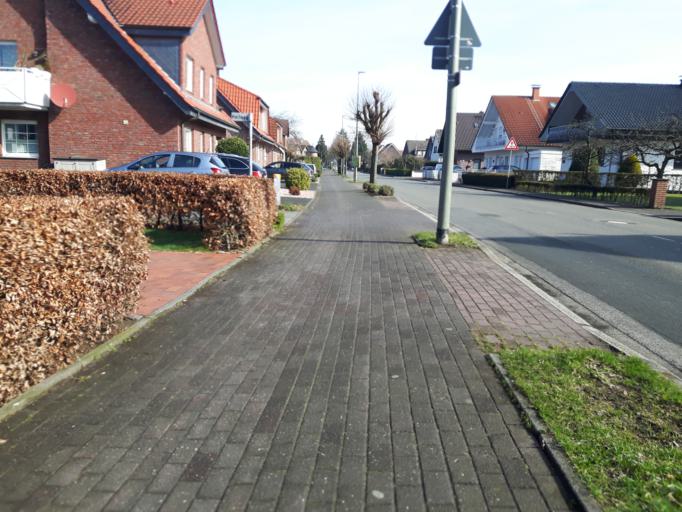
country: DE
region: North Rhine-Westphalia
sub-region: Regierungsbezirk Munster
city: Haltern
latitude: 51.7671
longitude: 7.2186
